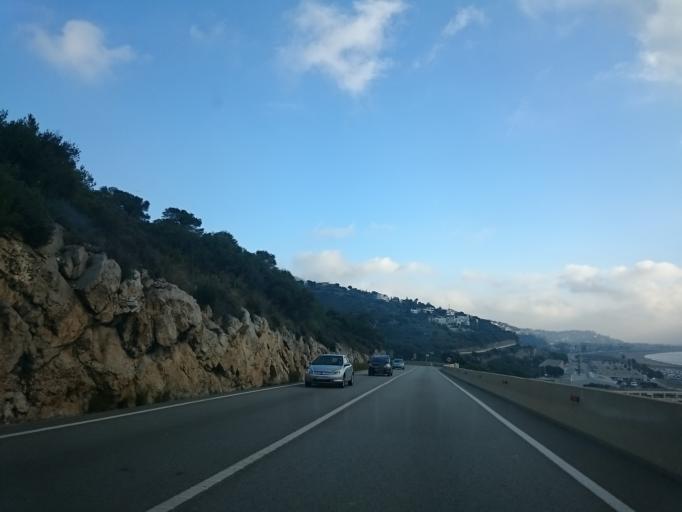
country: ES
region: Catalonia
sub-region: Provincia de Barcelona
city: Castelldefels
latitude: 41.2590
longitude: 1.9189
